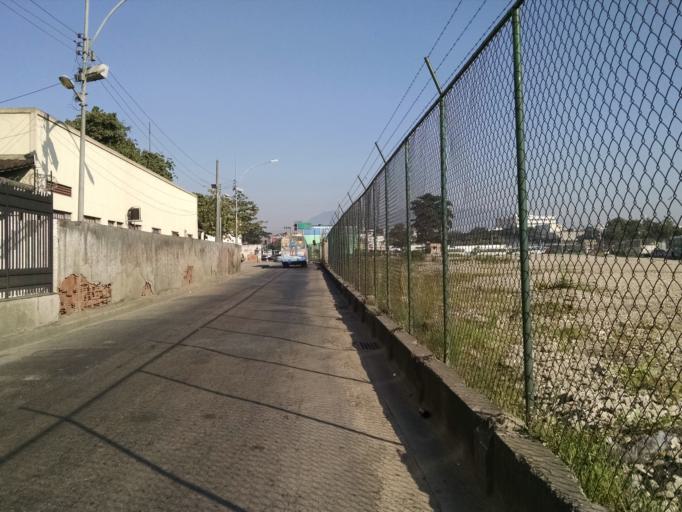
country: BR
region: Rio de Janeiro
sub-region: Sao Joao De Meriti
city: Sao Joao de Meriti
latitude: -22.8049
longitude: -43.3624
